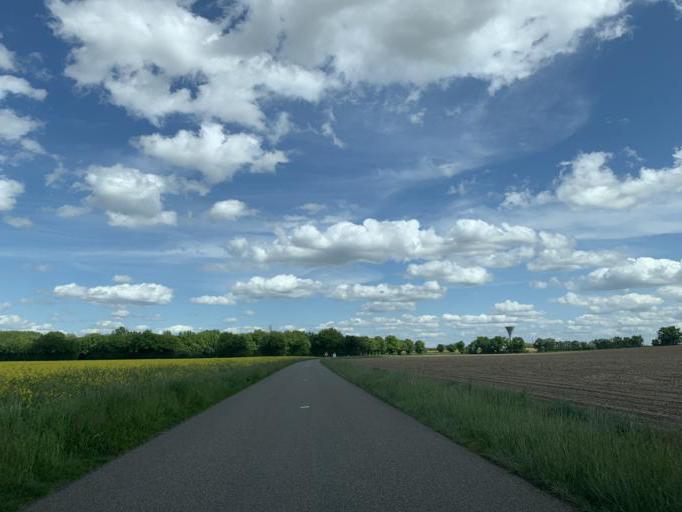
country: FR
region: Rhone-Alpes
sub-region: Departement de l'Ain
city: Ars-sur-Formans
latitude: 45.9745
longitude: 4.8437
